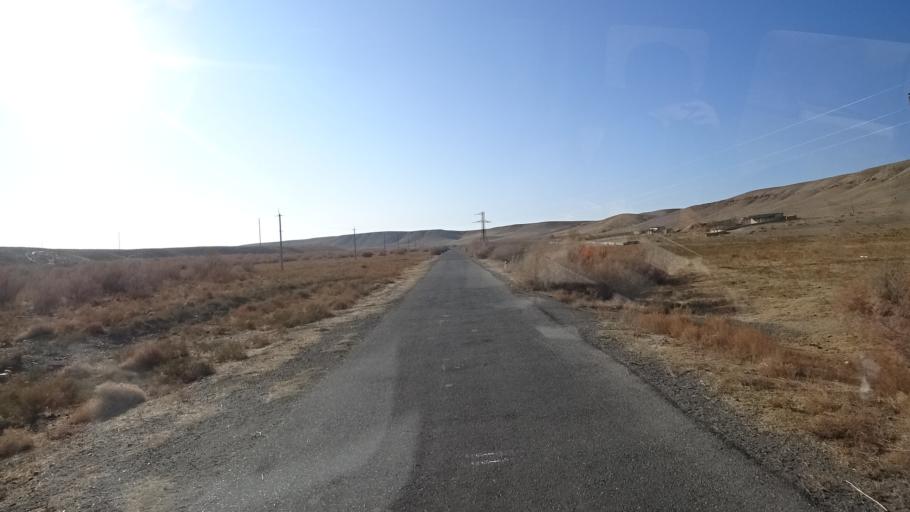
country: UZ
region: Navoiy
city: Beshrabot
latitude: 40.2574
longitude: 65.4489
